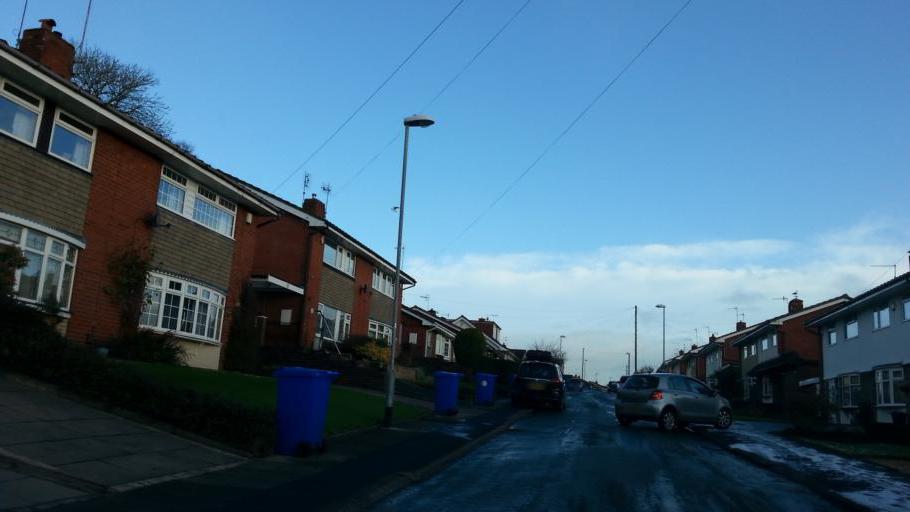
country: GB
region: England
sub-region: Staffordshire
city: Longton
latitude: 52.9821
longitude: -2.1526
